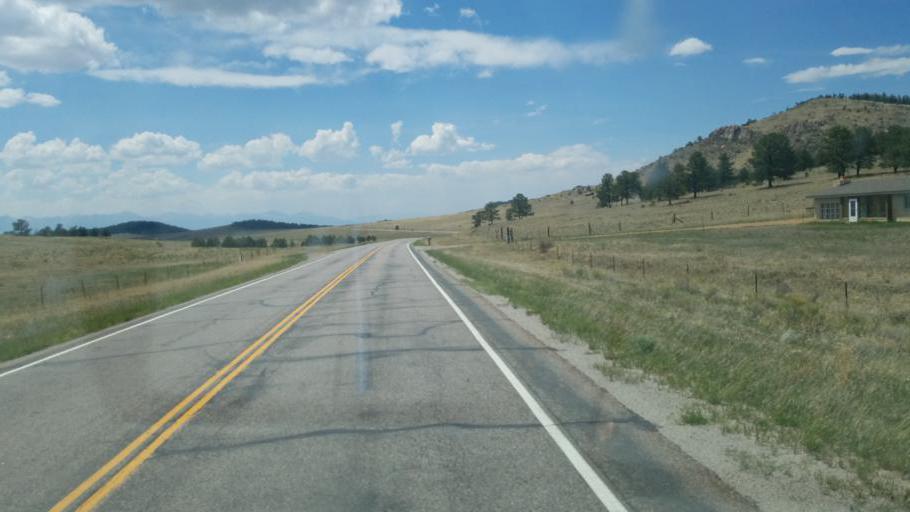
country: US
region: Colorado
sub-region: Custer County
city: Westcliffe
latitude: 38.1615
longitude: -105.2659
